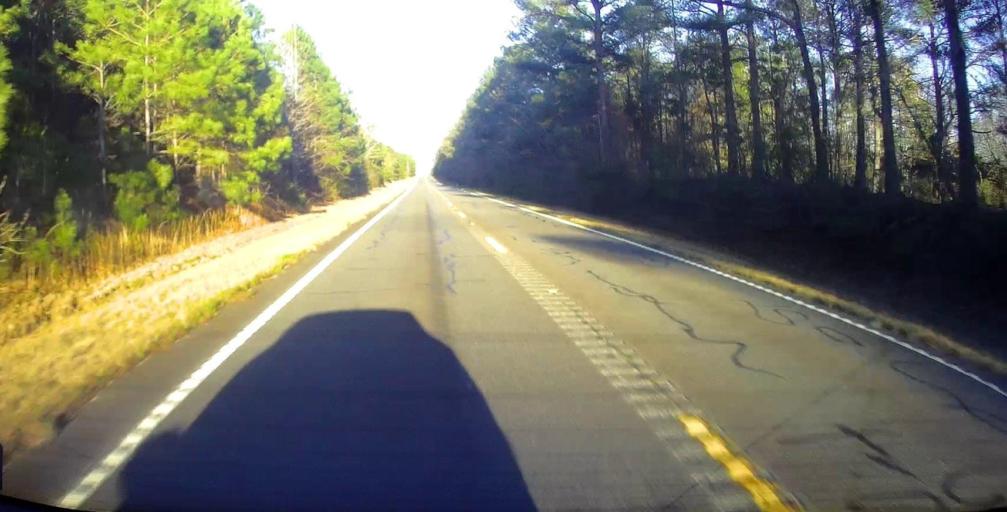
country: US
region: Georgia
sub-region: Talbot County
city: Talbotton
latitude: 32.6477
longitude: -84.6907
